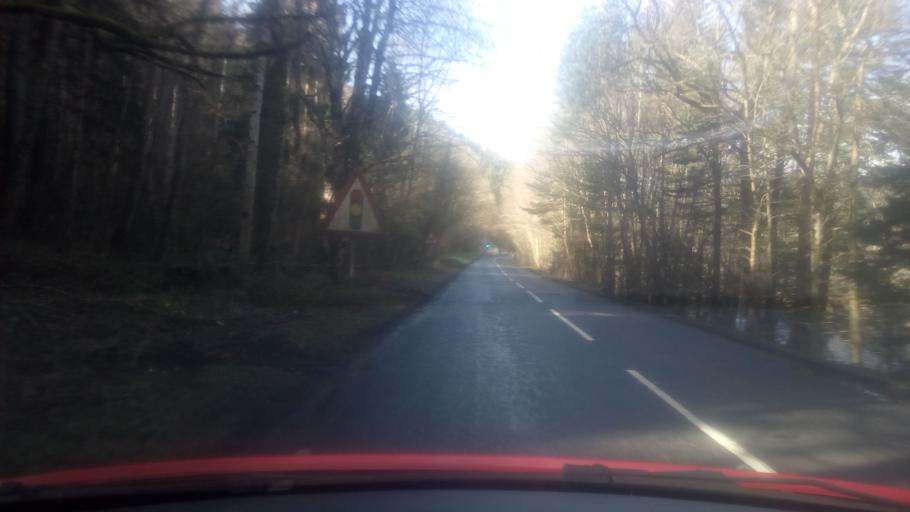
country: GB
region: Scotland
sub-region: The Scottish Borders
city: Selkirk
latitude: 55.5828
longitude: -2.8578
